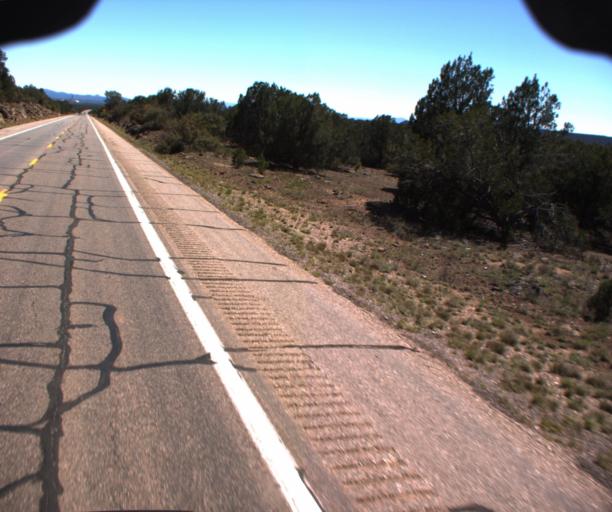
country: US
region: Arizona
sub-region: Yavapai County
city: Paulden
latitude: 35.0664
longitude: -112.4004
